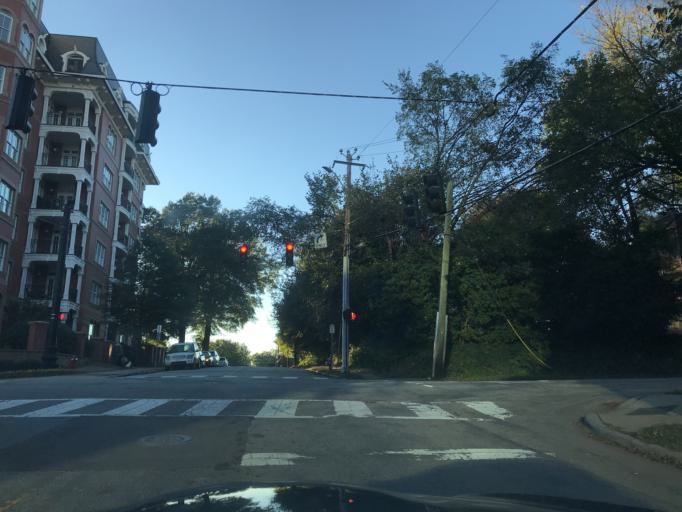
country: US
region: North Carolina
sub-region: Wake County
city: Raleigh
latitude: 35.7786
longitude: -78.6490
